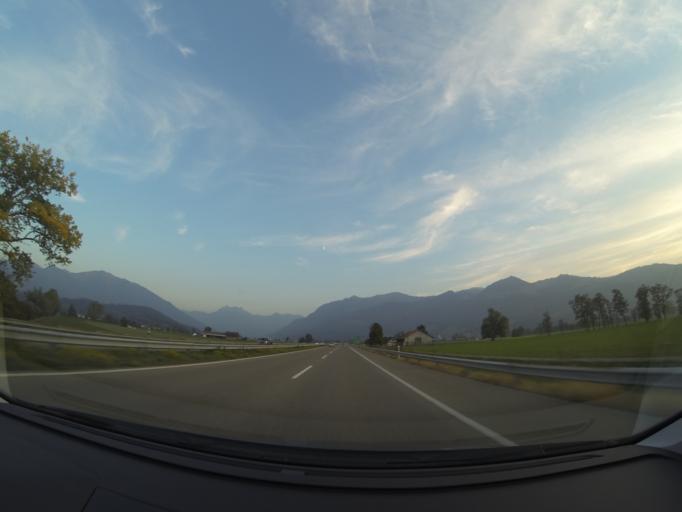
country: CH
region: Schwyz
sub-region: Bezirk March
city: Tuggen
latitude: 47.1970
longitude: 8.9704
